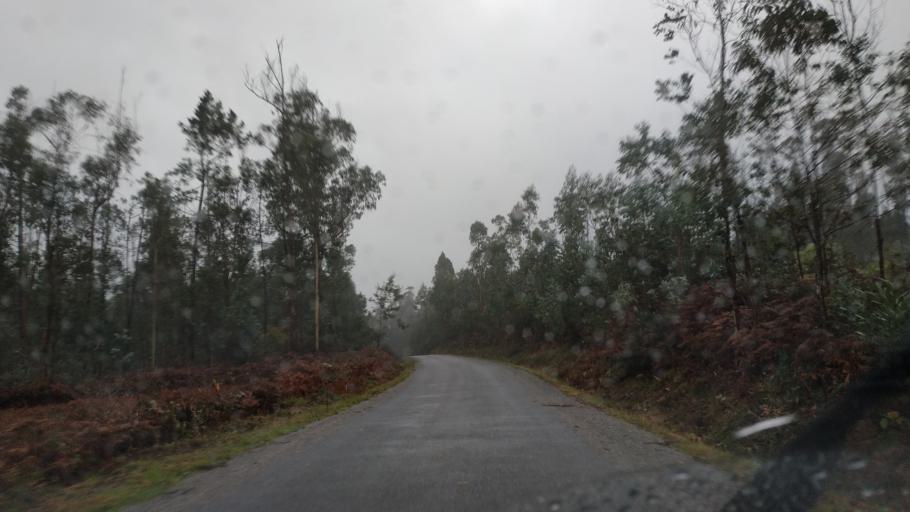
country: ES
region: Galicia
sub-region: Provincia da Coruna
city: Negreira
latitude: 42.9102
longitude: -8.7676
